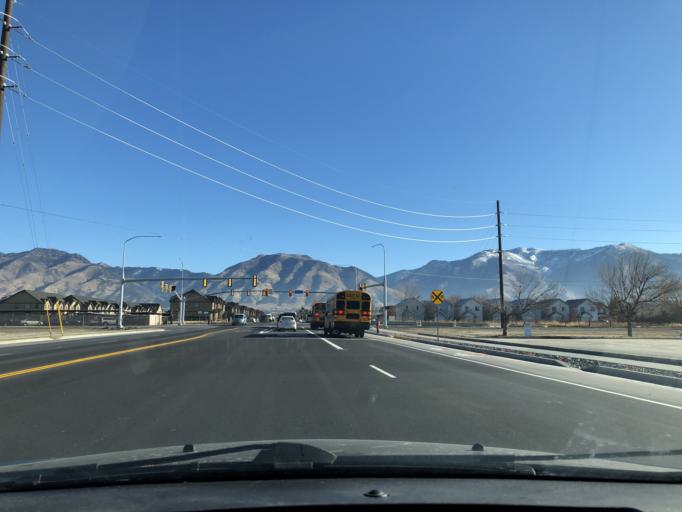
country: US
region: Utah
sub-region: Cache County
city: Logan
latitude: 41.7579
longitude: -111.8503
